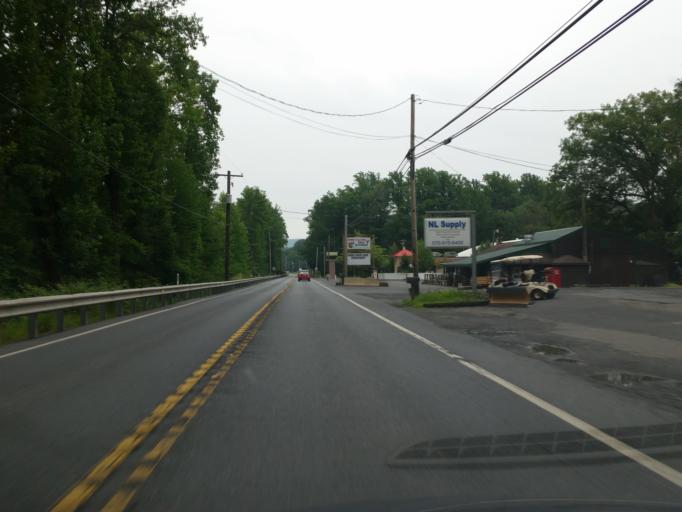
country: US
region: Pennsylvania
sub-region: Schuylkill County
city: Pine Grove
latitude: 40.5668
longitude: -76.4010
